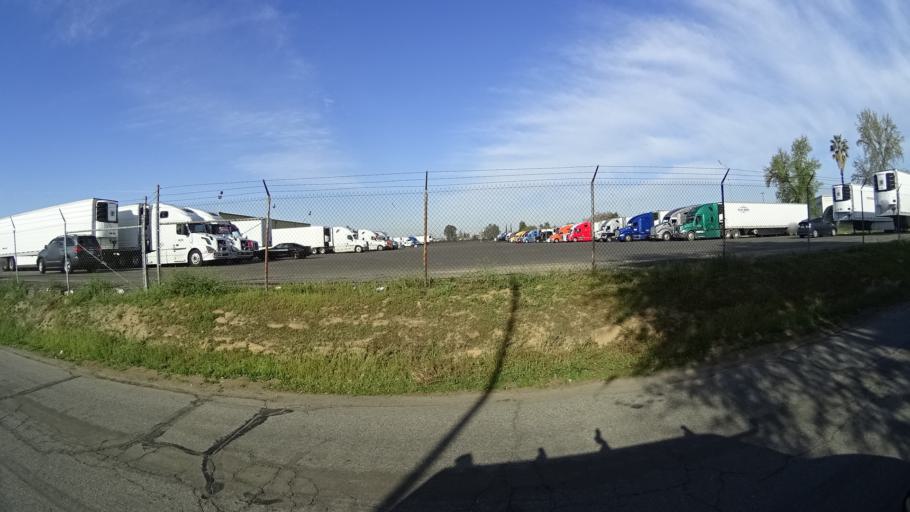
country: US
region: California
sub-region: Fresno County
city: West Park
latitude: 36.8131
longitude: -119.8806
